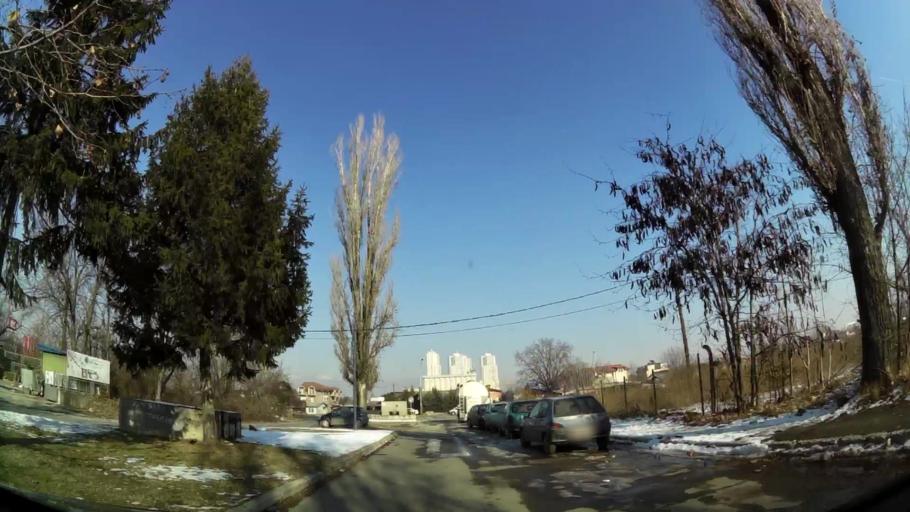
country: MK
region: Kisela Voda
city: Usje
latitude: 41.9723
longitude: 21.4583
